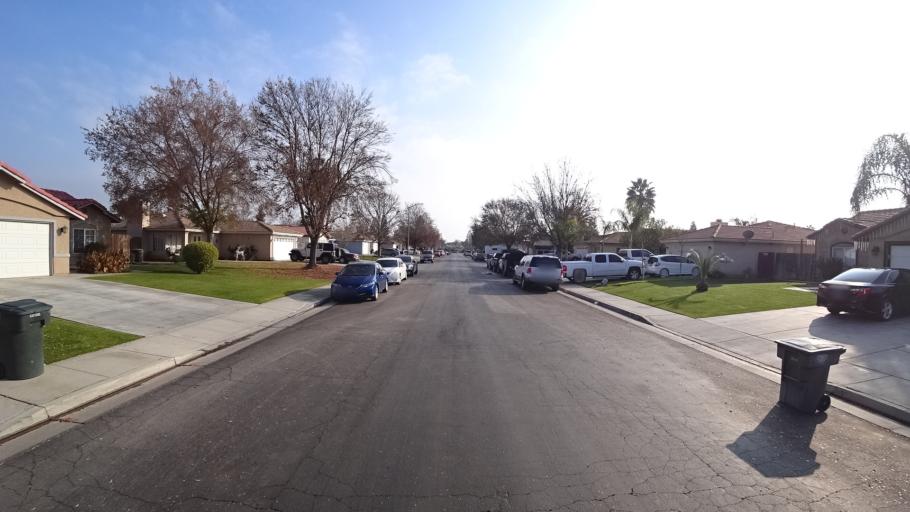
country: US
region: California
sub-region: Kern County
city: Greenfield
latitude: 35.3054
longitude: -119.0683
